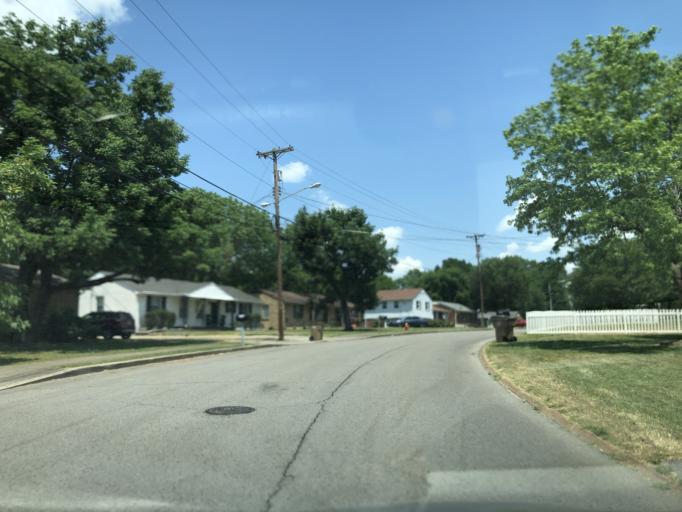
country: US
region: Tennessee
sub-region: Davidson County
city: Goodlettsville
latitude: 36.2709
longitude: -86.7012
